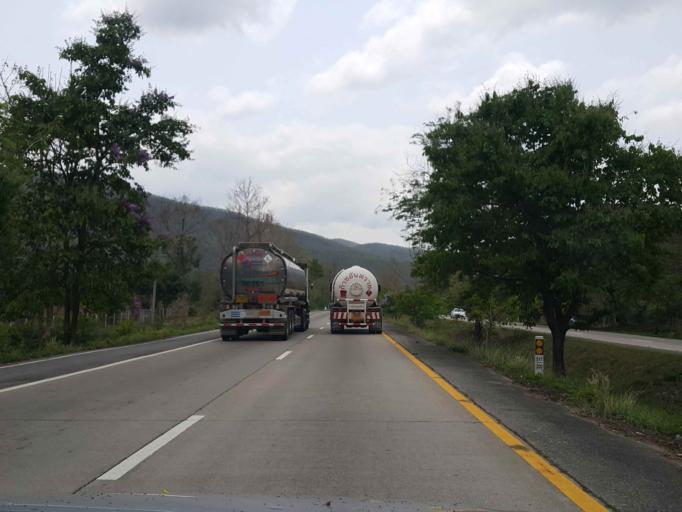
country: TH
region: Lamphun
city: Mae Tha
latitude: 18.5082
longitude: 99.1295
